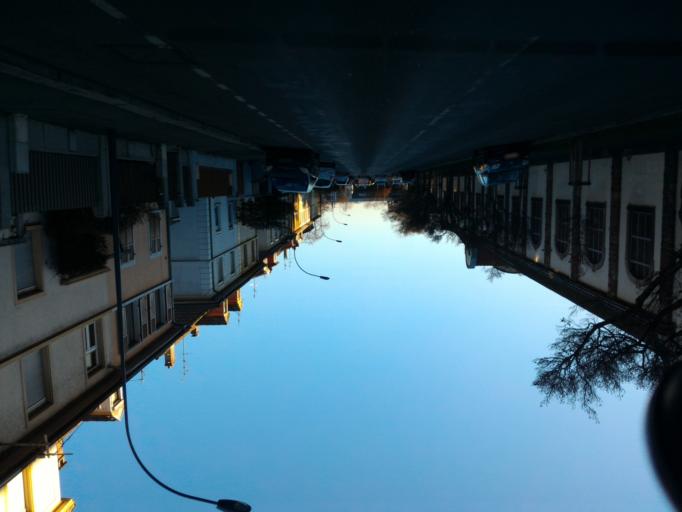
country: FR
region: Alsace
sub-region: Departement du Haut-Rhin
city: Riedisheim
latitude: 47.7619
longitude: 7.3600
